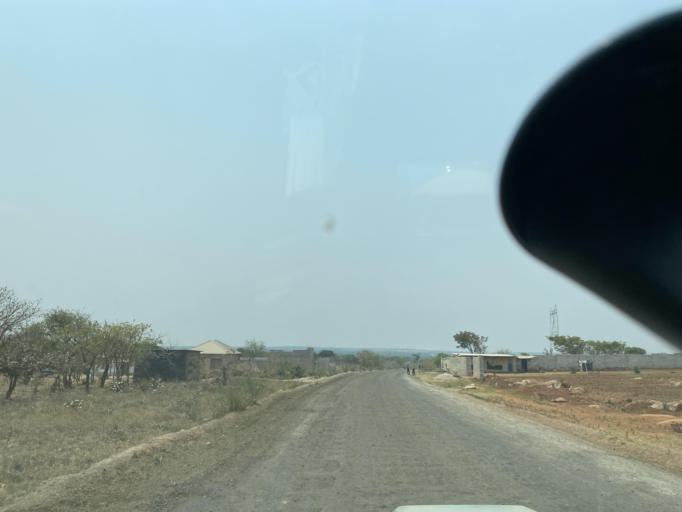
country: ZM
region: Lusaka
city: Lusaka
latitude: -15.5435
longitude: 28.4455
